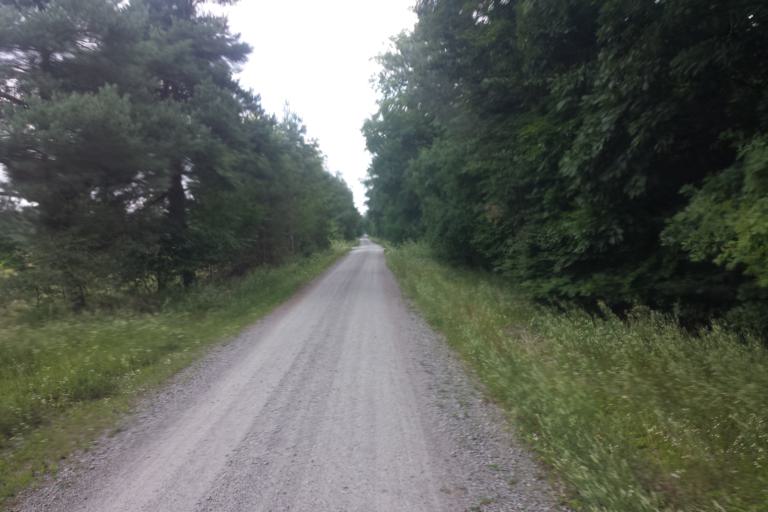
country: DE
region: Hesse
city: Viernheim
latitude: 49.5669
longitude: 8.5269
